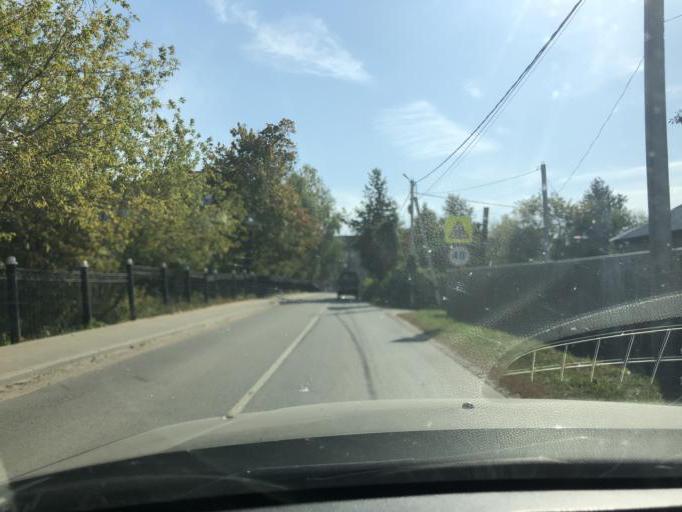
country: RU
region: Tula
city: Yasnogorsk
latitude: 54.4837
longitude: 37.6950
